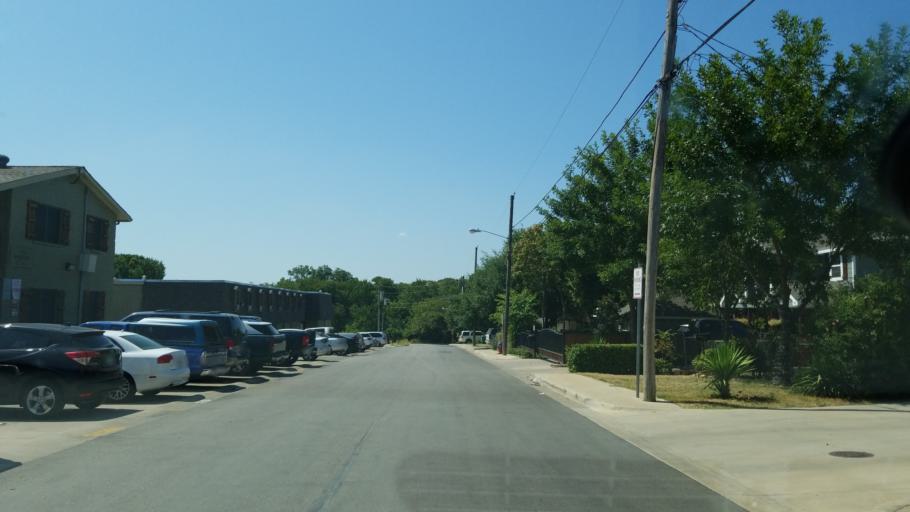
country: US
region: Texas
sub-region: Dallas County
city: Cockrell Hill
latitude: 32.7415
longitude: -96.8825
